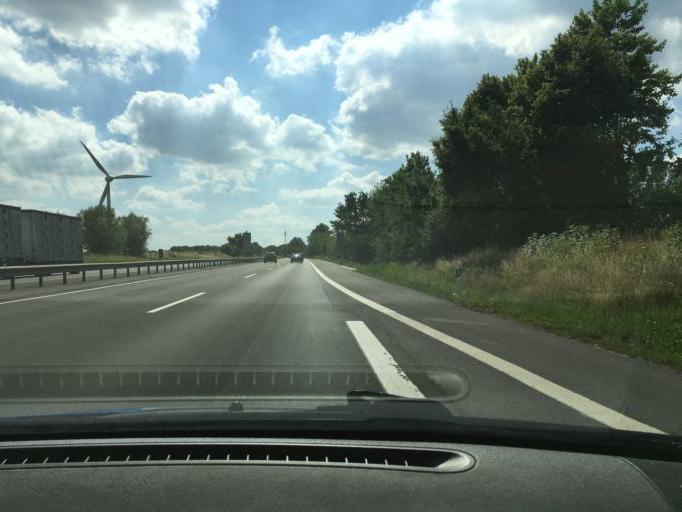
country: DE
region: Lower Saxony
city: Seevetal
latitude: 53.3995
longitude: 9.8985
